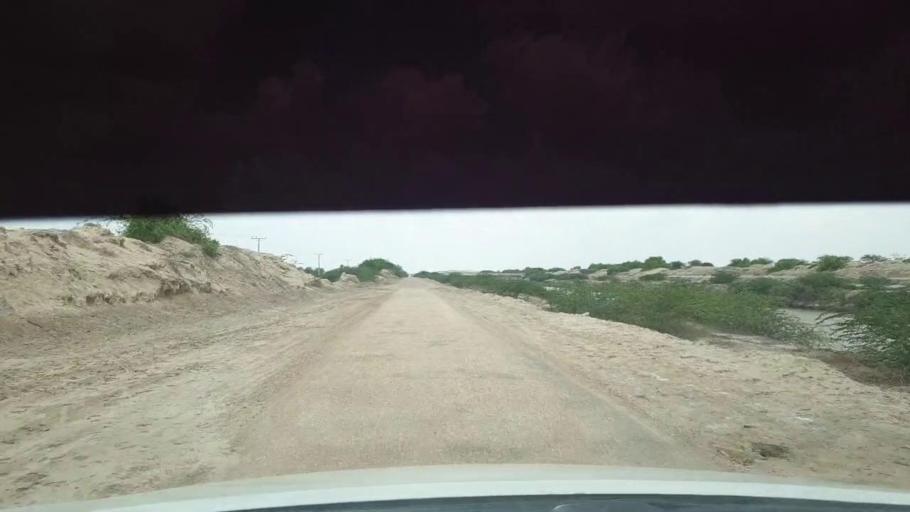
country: PK
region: Sindh
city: Kadhan
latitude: 24.4961
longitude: 69.1038
